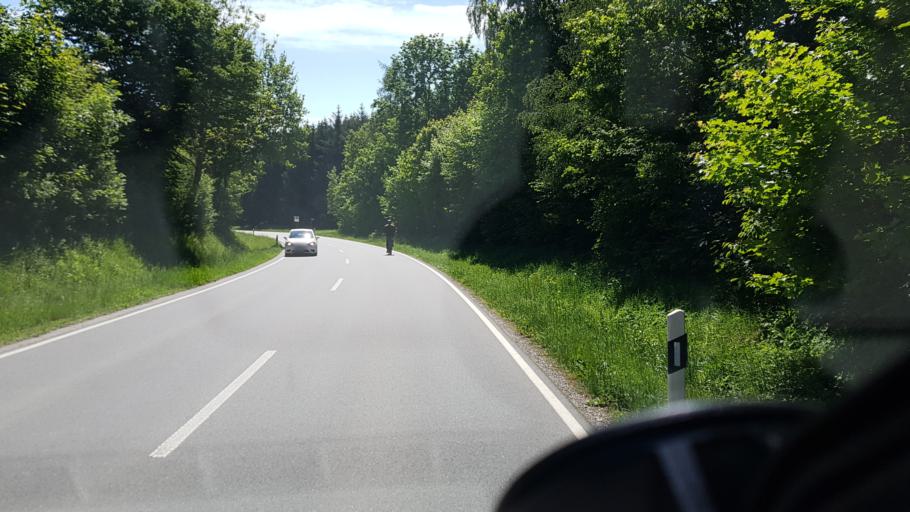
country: DE
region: Bavaria
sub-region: Lower Bavaria
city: Triftern
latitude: 48.4031
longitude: 12.9843
